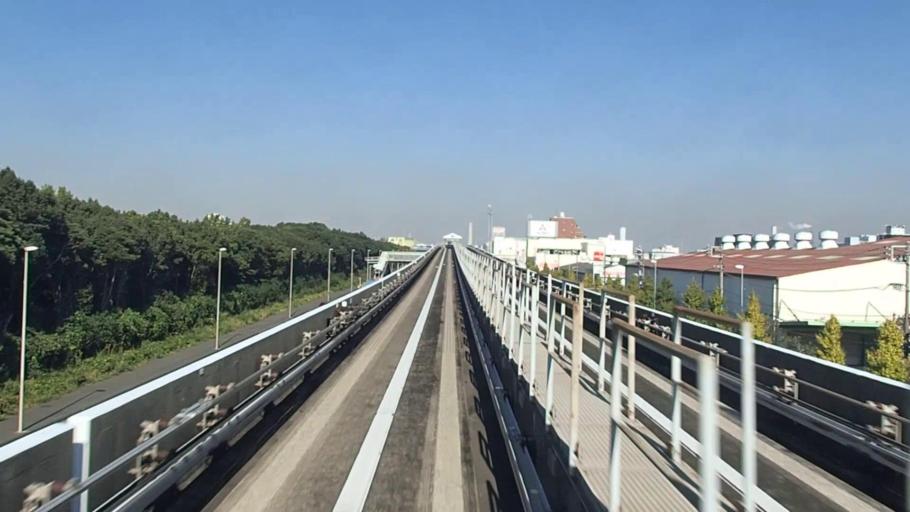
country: JP
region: Kanagawa
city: Yokosuka
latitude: 35.3555
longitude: 139.6439
